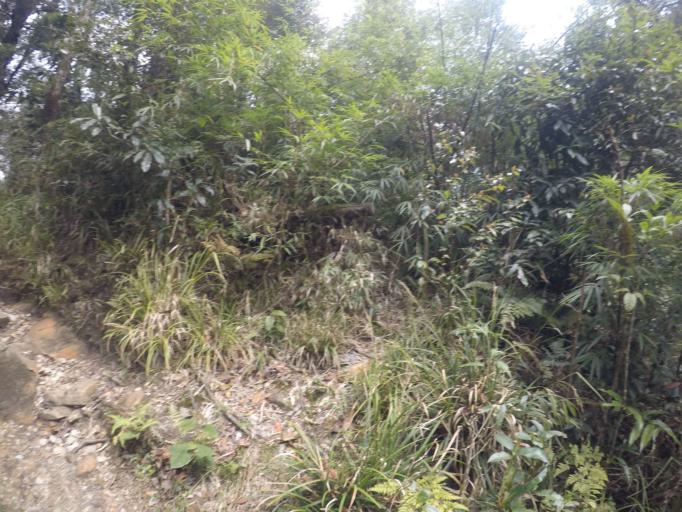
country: VN
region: Lao Cai
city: Sa Pa
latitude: 22.3474
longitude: 103.7737
